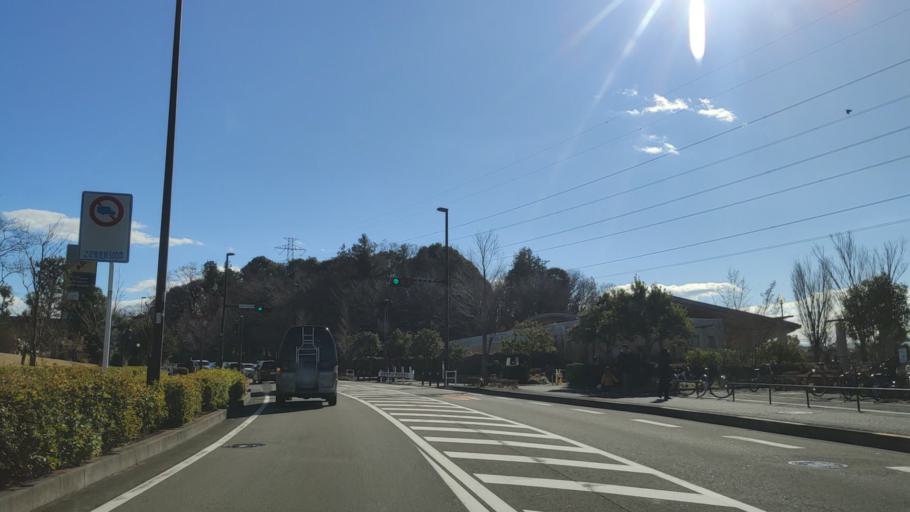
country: JP
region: Tokyo
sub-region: Machida-shi
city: Machida
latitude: 35.5190
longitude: 139.4962
